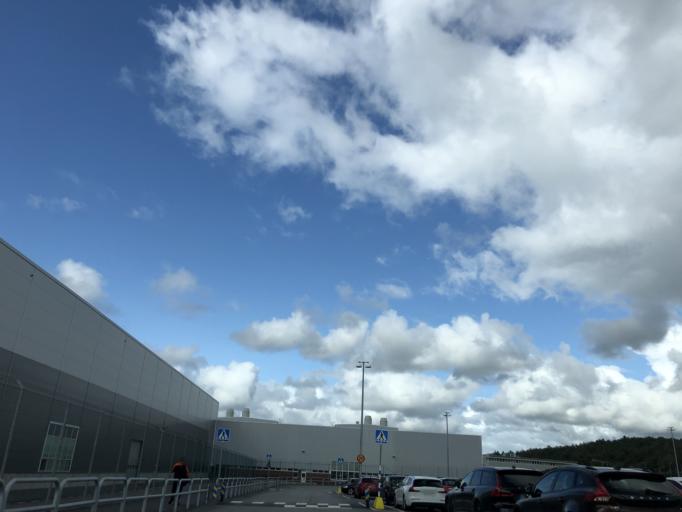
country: SE
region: Vaestra Goetaland
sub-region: Goteborg
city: Torslanda
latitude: 57.7224
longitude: 11.8440
